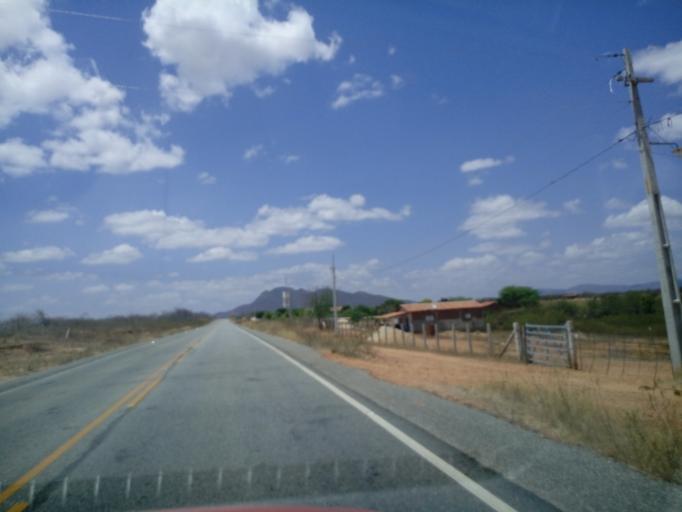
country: BR
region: Paraiba
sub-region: Patos
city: Patos
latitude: -7.0276
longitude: -37.1705
